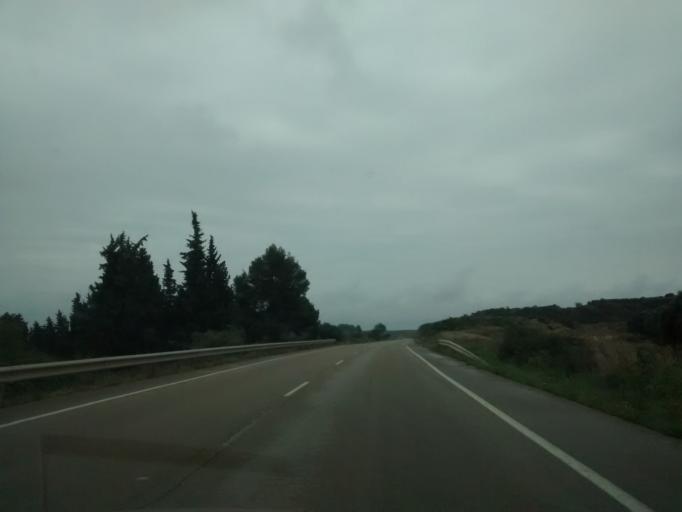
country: ES
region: Aragon
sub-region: Provincia de Zaragoza
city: Caspe
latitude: 41.2173
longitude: -0.0129
